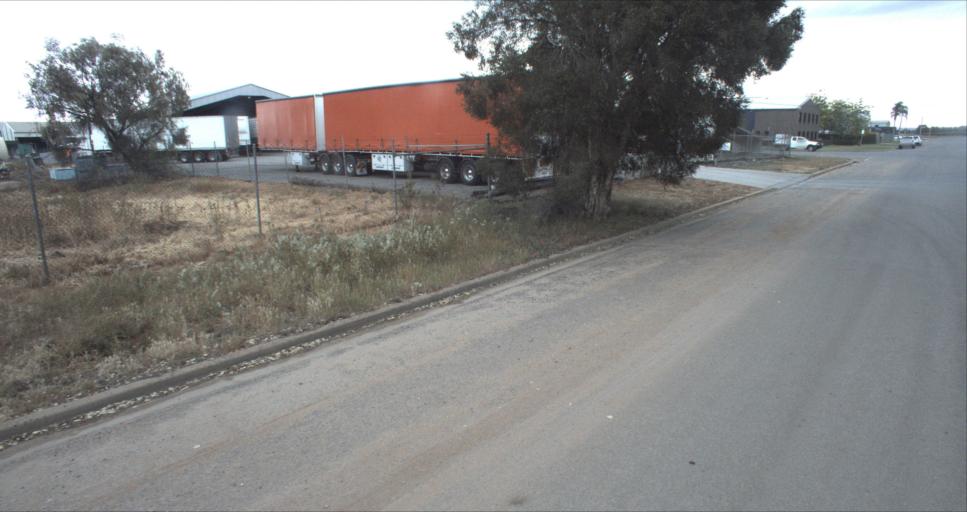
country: AU
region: New South Wales
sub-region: Leeton
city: Leeton
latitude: -34.5493
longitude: 146.3905
